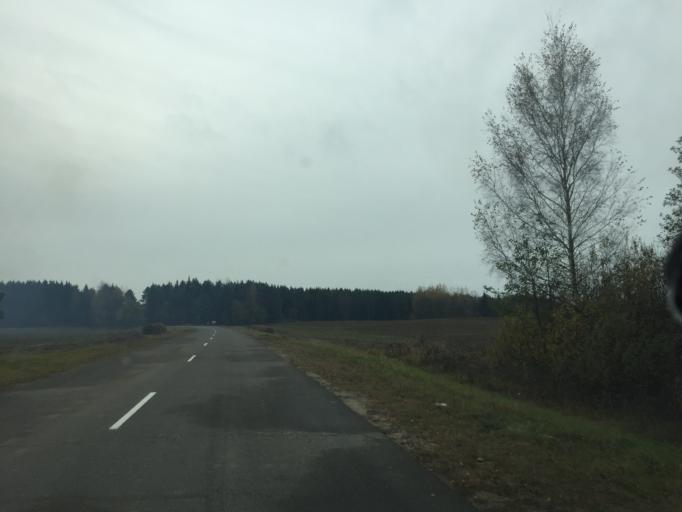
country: BY
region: Mogilev
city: Drybin
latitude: 54.0131
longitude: 31.0214
